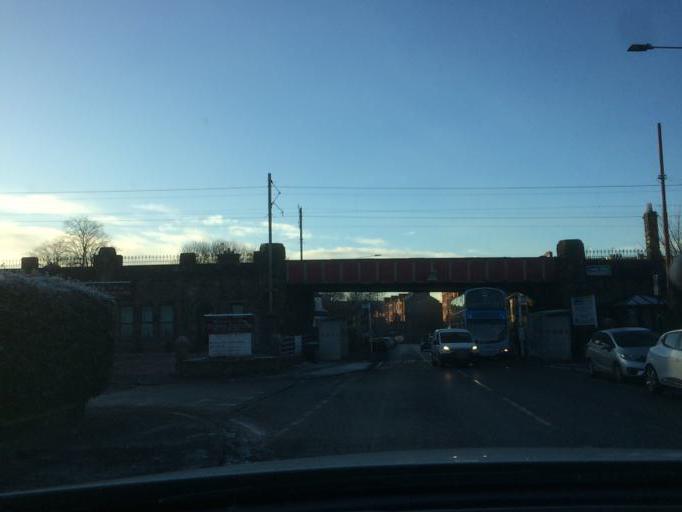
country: GB
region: Scotland
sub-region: East Renfrewshire
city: Giffnock
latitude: 55.8283
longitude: -4.2909
